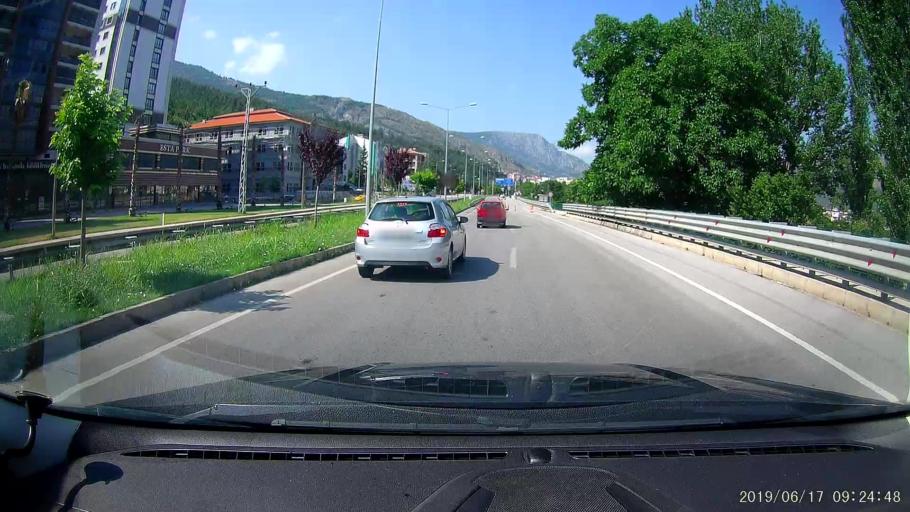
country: TR
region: Amasya
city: Amasya
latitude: 40.6701
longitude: 35.8535
